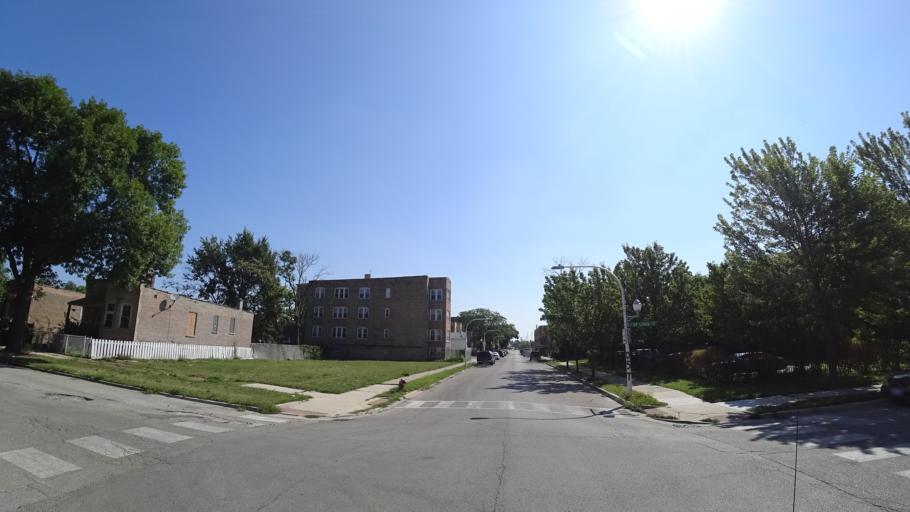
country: US
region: Illinois
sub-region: Cook County
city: Cicero
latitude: 41.8673
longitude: -87.7131
